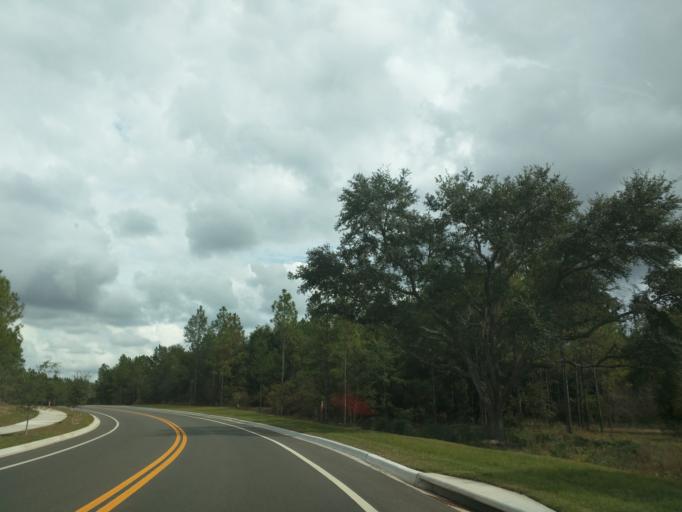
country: US
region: Florida
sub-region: Leon County
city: Woodville
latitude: 30.3814
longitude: -84.2134
